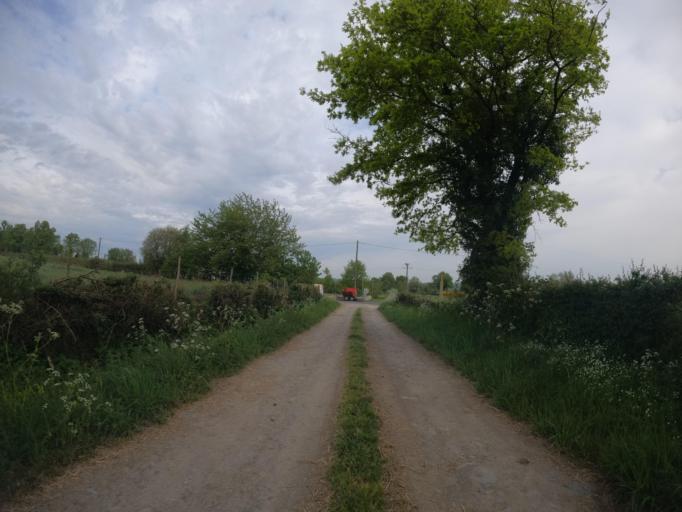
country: FR
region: Poitou-Charentes
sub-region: Departement des Deux-Sevres
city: La Chapelle-Saint-Laurent
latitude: 46.7062
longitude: -0.4812
